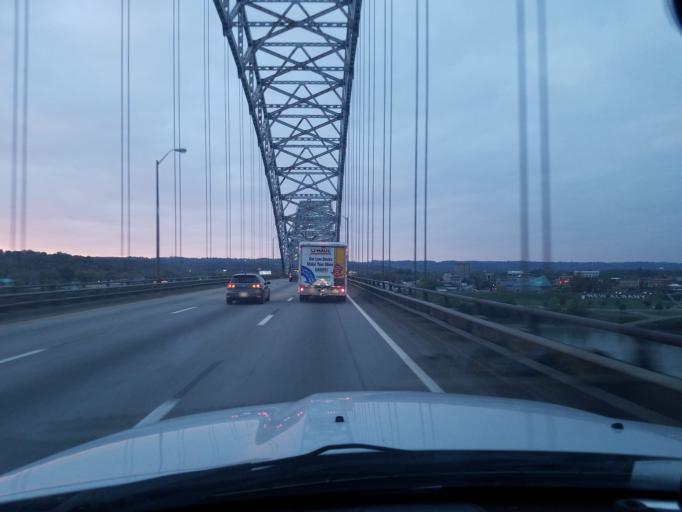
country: US
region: Indiana
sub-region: Floyd County
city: New Albany
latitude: 38.2773
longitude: -85.8206
